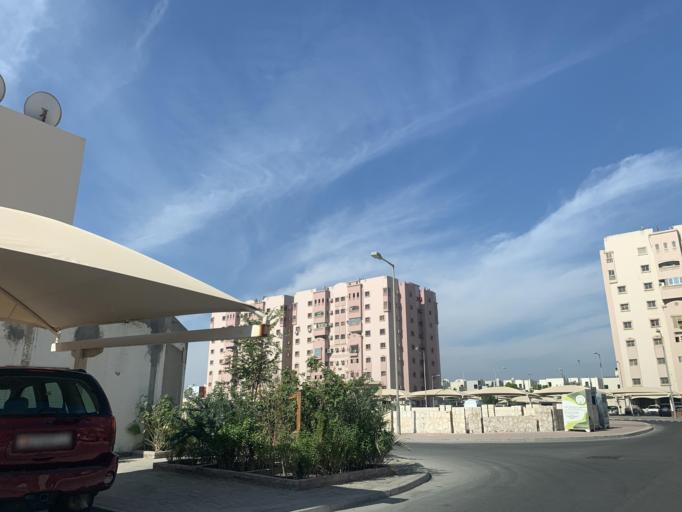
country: BH
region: Central Governorate
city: Madinat Hamad
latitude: 26.1195
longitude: 50.4867
